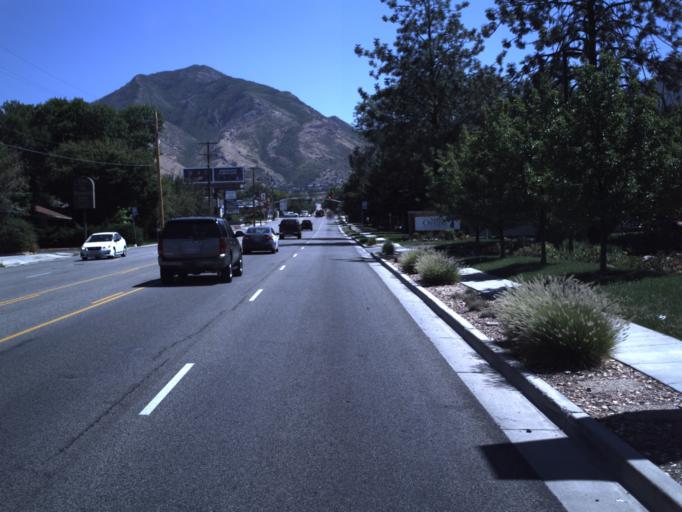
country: US
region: Utah
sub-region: Salt Lake County
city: Canyon Rim
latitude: 40.6998
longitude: -111.8283
